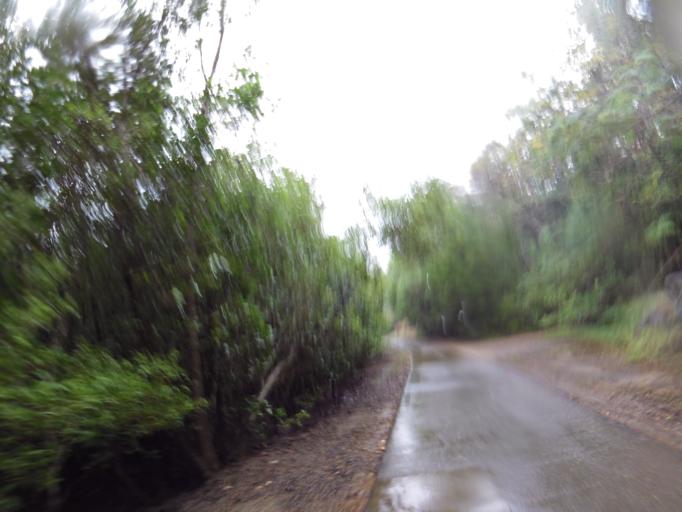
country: AU
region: Queensland
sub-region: Cairns
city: Cairns
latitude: -16.8972
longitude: 145.7534
